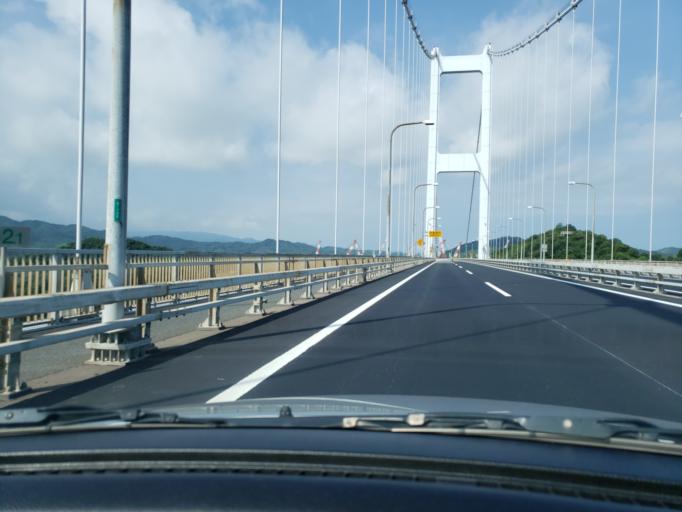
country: JP
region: Hiroshima
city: Takehara
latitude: 34.1144
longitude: 132.9824
